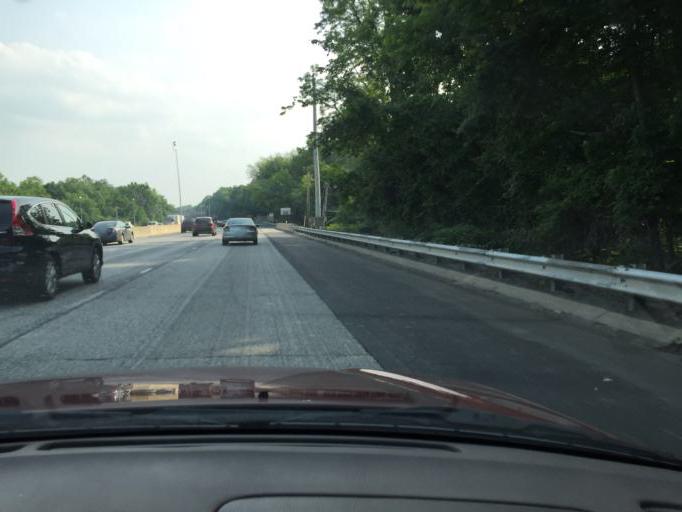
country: US
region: New York
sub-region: Westchester County
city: Mamaroneck
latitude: 40.9526
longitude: -73.7452
